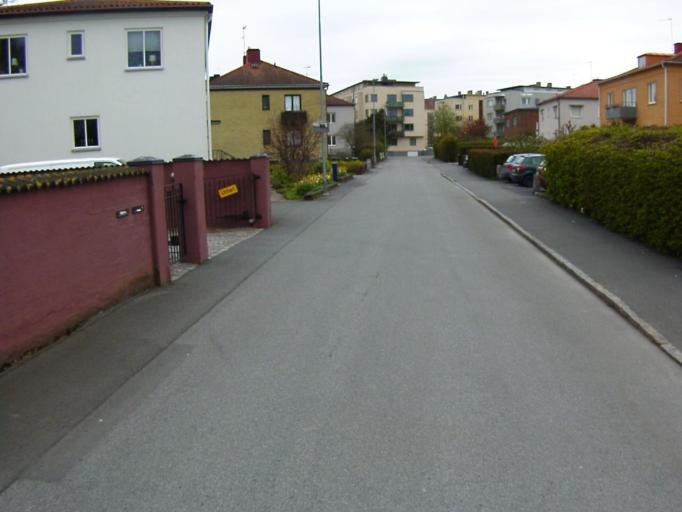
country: SE
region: Skane
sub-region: Kristianstads Kommun
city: Kristianstad
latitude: 56.0253
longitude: 14.1667
